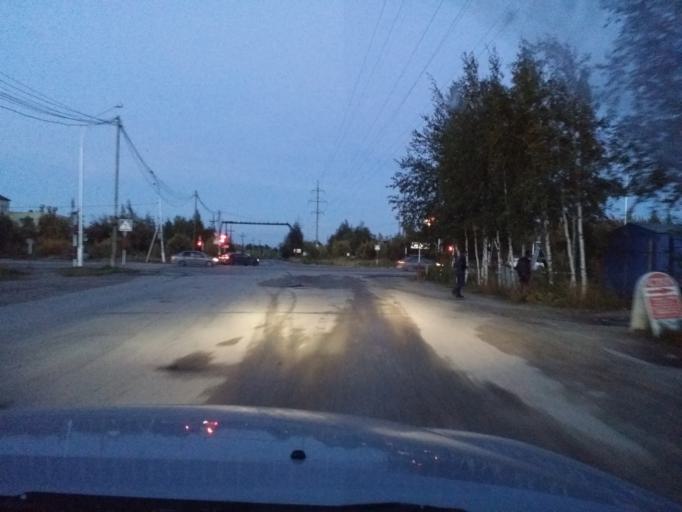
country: RU
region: Khanty-Mansiyskiy Avtonomnyy Okrug
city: Nizhnevartovsk
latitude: 60.9594
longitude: 76.5291
